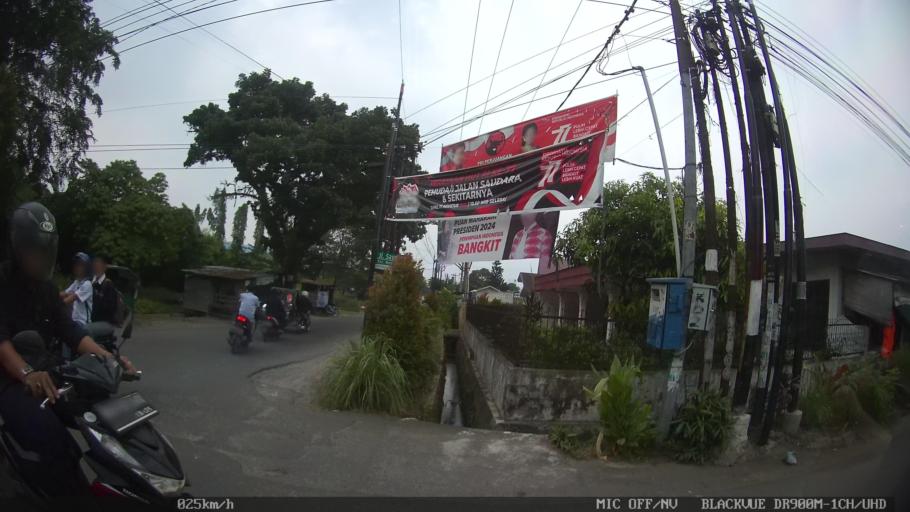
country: ID
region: North Sumatra
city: Medan
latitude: 3.5569
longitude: 98.7029
